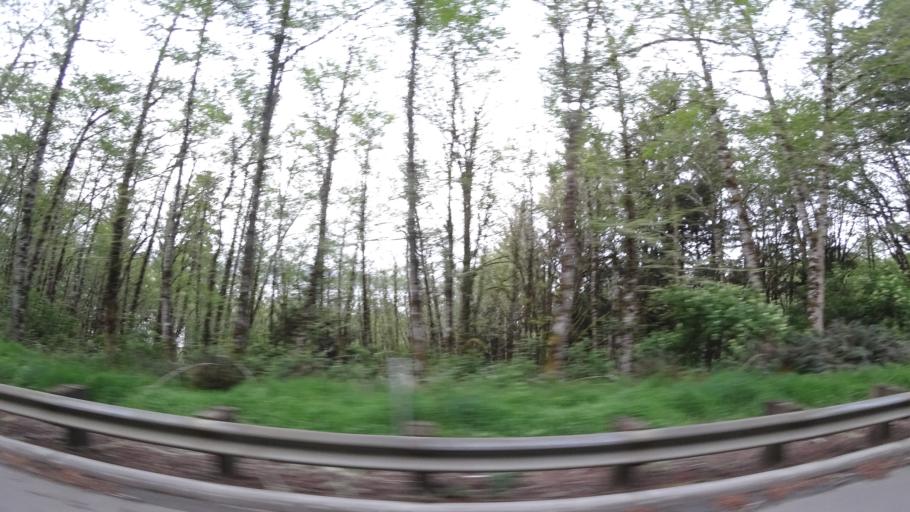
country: US
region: Oregon
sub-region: Douglas County
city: Reedsport
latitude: 43.7512
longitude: -124.1240
